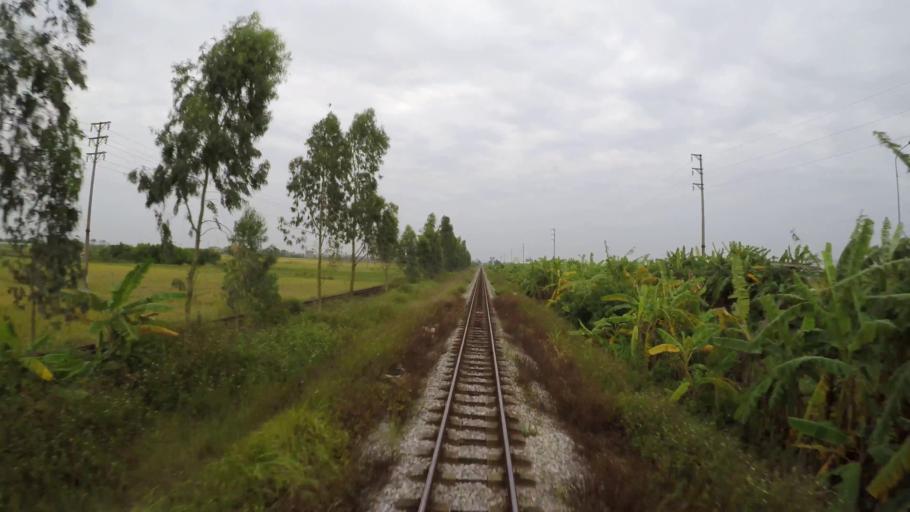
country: VN
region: Hai Duong
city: Lai Cach
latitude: 20.9471
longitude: 106.2613
